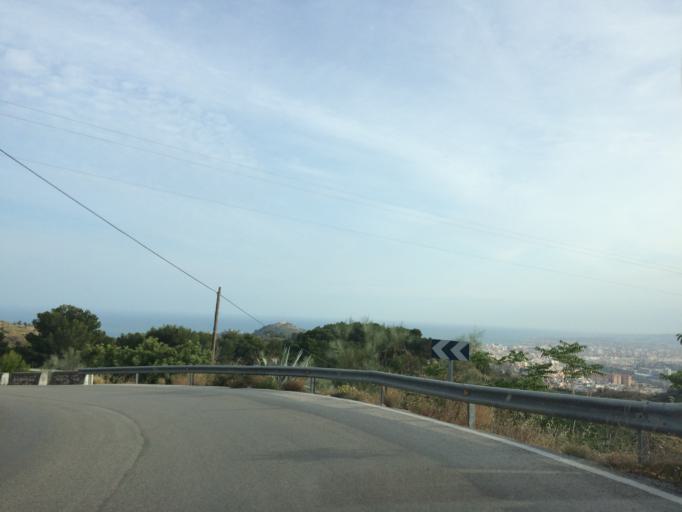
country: ES
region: Andalusia
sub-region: Provincia de Malaga
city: Malaga
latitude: 36.7589
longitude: -4.4080
